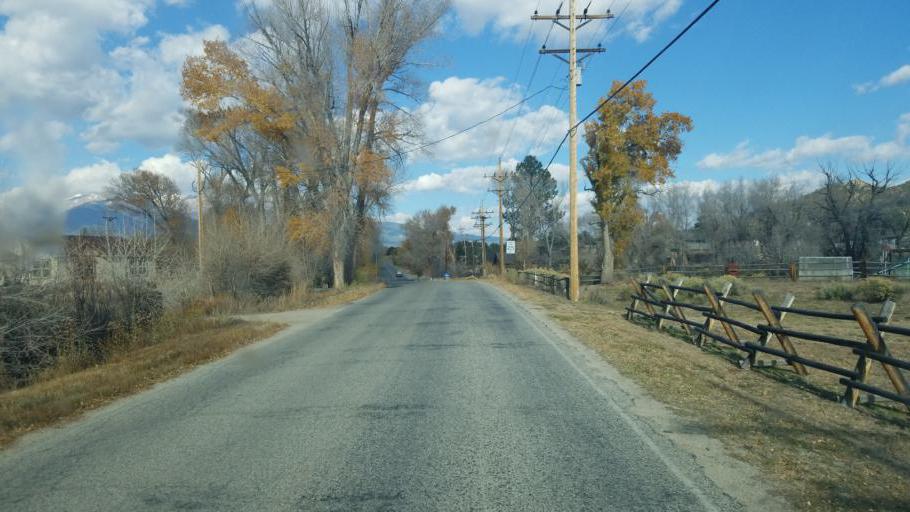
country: US
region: Colorado
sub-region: Chaffee County
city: Buena Vista
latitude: 38.8353
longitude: -106.1176
